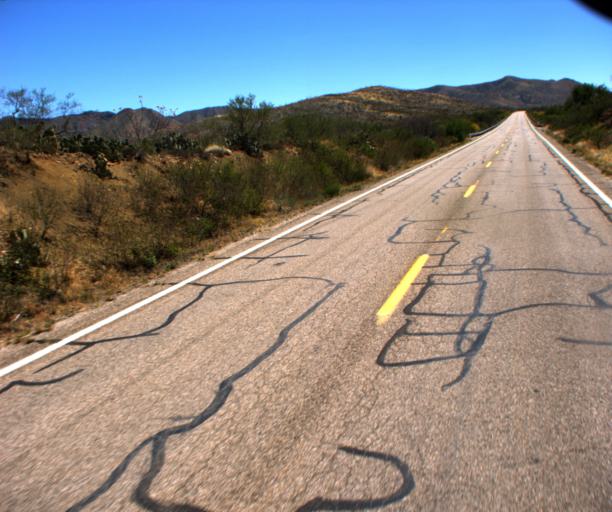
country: US
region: Arizona
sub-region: Pima County
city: Corona de Tucson
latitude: 31.9367
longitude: -110.6612
